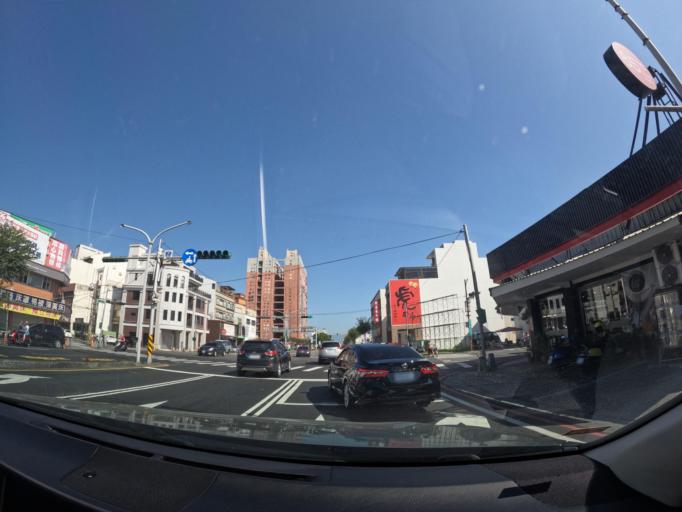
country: TW
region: Taiwan
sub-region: Yilan
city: Yilan
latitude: 24.6744
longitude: 121.7778
